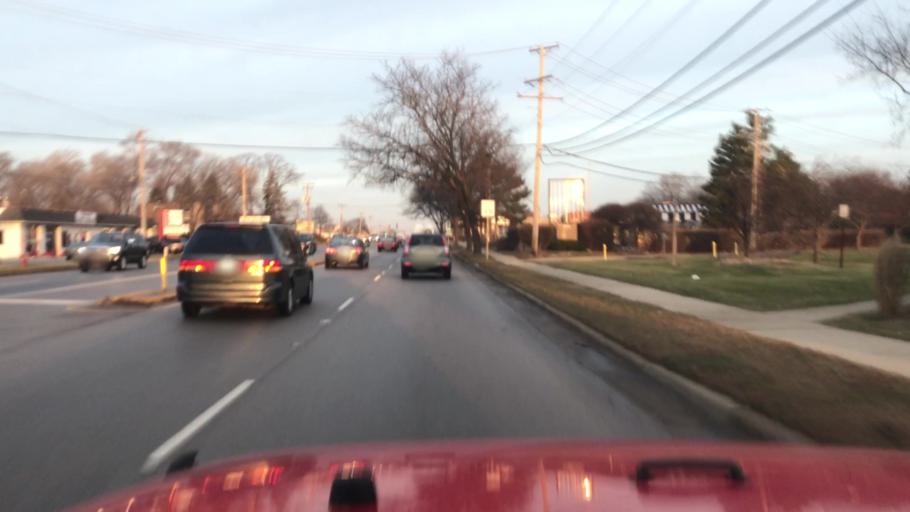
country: US
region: Illinois
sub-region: Cook County
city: Arlington Heights
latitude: 42.1030
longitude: -87.9659
